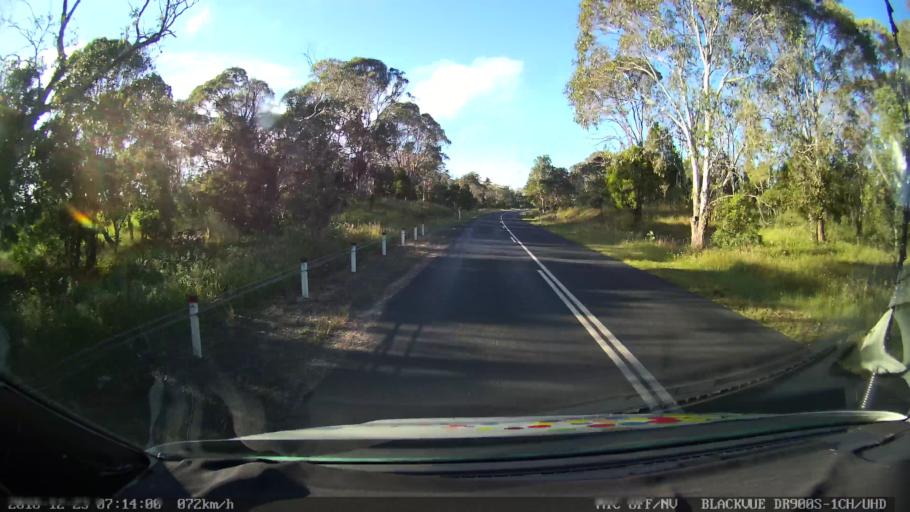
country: AU
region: New South Wales
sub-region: Bellingen
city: Dorrigo
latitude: -30.4304
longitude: 152.3247
